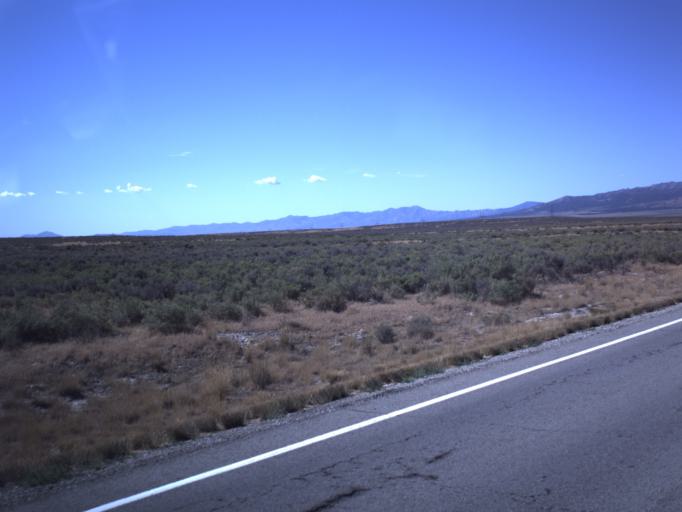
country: US
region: Utah
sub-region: Tooele County
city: Tooele
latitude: 40.3716
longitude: -112.4001
